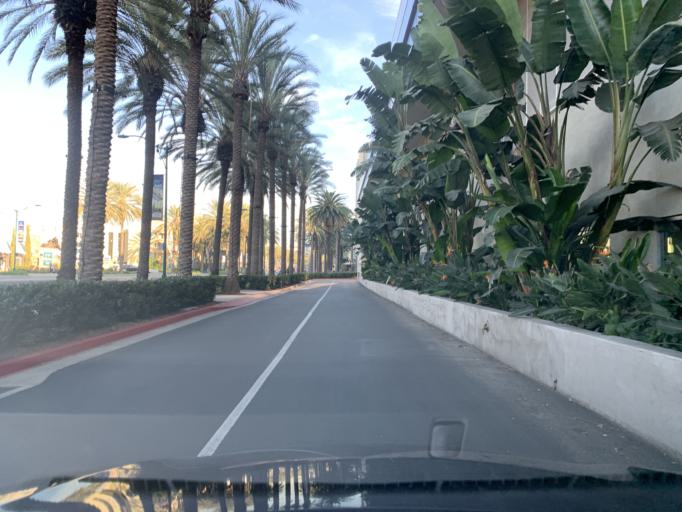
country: US
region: California
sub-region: Orange County
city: Anaheim
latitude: 33.8031
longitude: -117.9186
